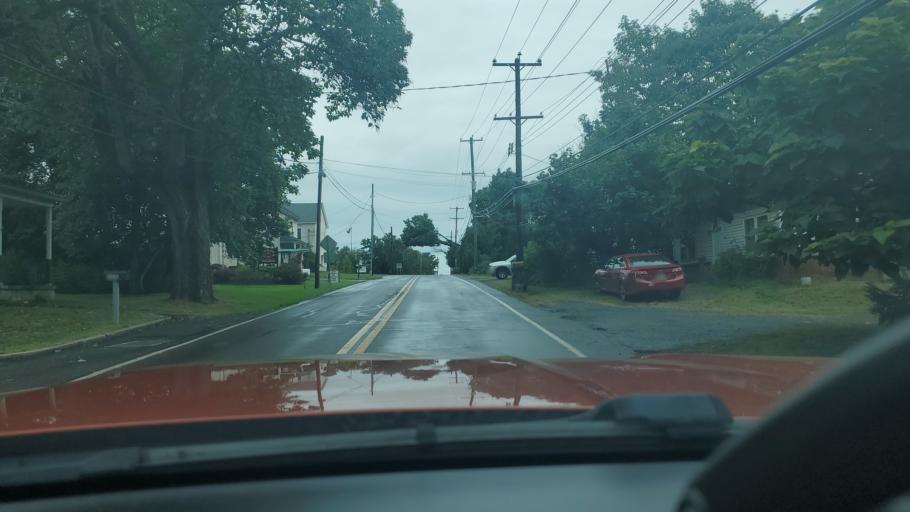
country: US
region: Pennsylvania
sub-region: Montgomery County
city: Spring Mount
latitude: 40.2784
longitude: -75.4806
